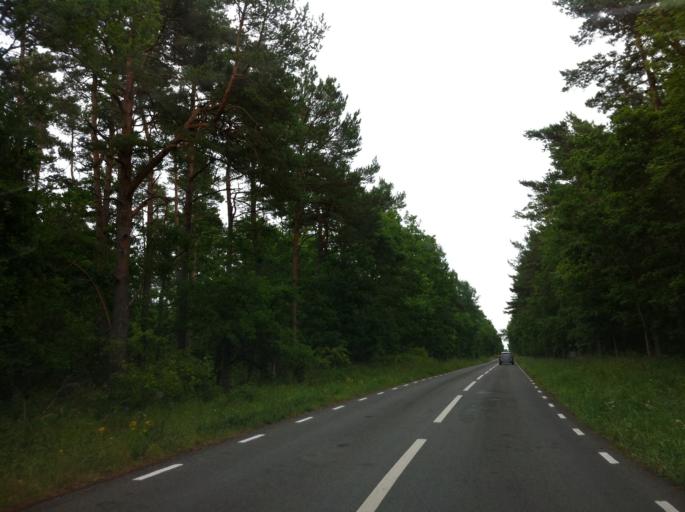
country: SE
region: Kalmar
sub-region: Vasterviks Kommun
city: Vaestervik
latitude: 57.3546
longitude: 17.0575
